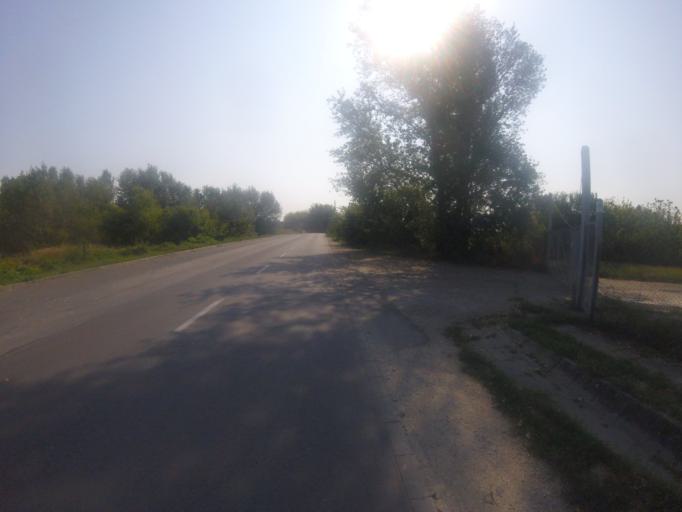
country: HU
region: Bacs-Kiskun
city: Baja
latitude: 46.1906
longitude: 18.9322
